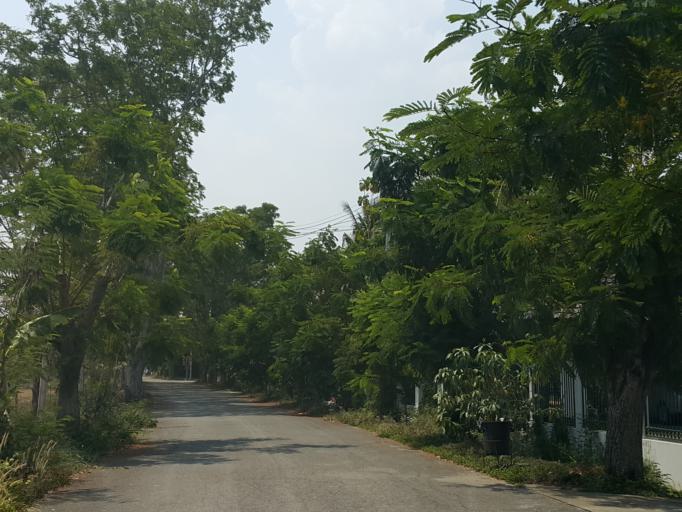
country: TH
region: Chiang Mai
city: Chiang Mai
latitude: 18.7317
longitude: 98.9755
